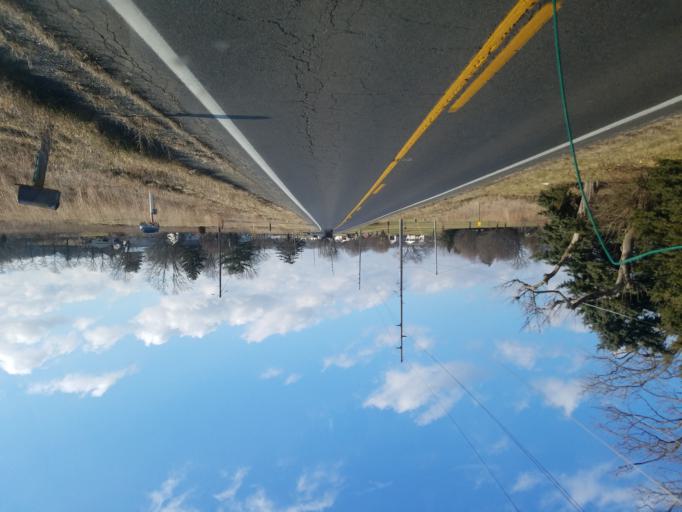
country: US
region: Ohio
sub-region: Marion County
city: Marion
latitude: 40.5611
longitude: -83.1712
